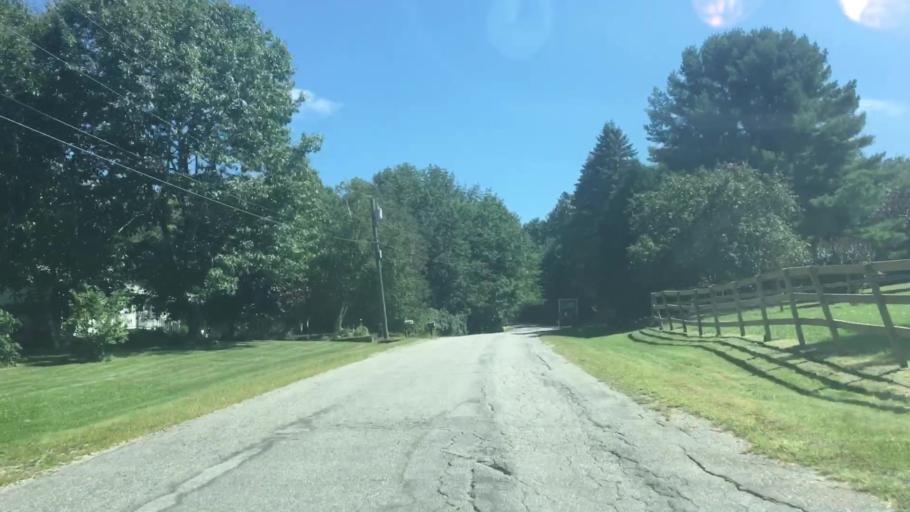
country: US
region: Maine
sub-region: Androscoggin County
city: Sabattus
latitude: 44.1224
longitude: -70.0609
